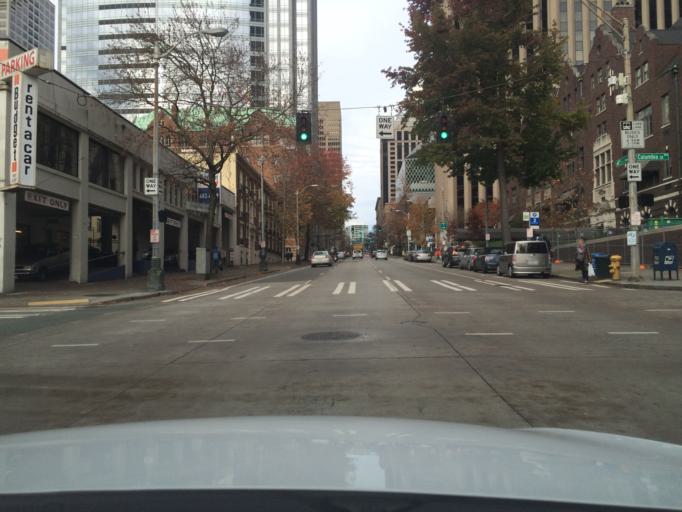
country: US
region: Washington
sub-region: King County
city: Seattle
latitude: 47.6045
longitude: -122.3315
